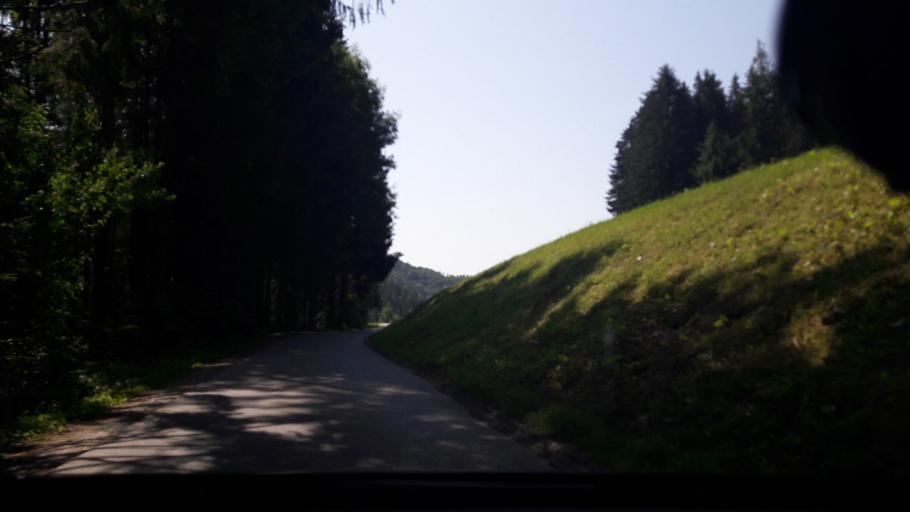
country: AT
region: Styria
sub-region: Politischer Bezirk Voitsberg
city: Sodingberg
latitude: 47.1107
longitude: 15.1887
